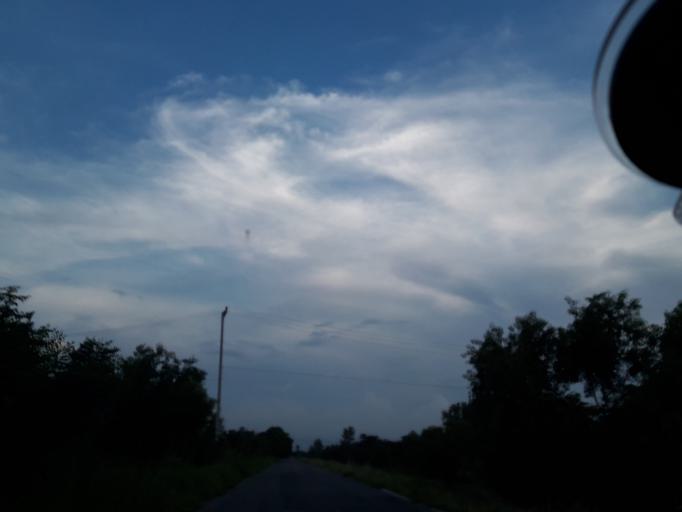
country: TH
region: Pathum Thani
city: Nong Suea
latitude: 14.2182
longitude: 100.8689
